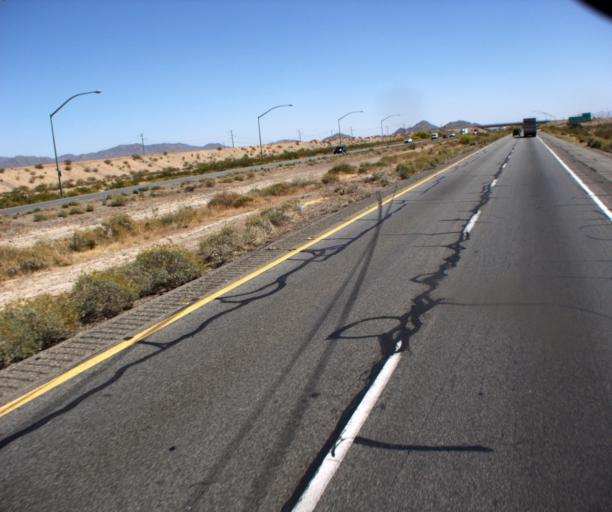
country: US
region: Arizona
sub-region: Maricopa County
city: Buckeye
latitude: 33.4410
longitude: -112.6861
